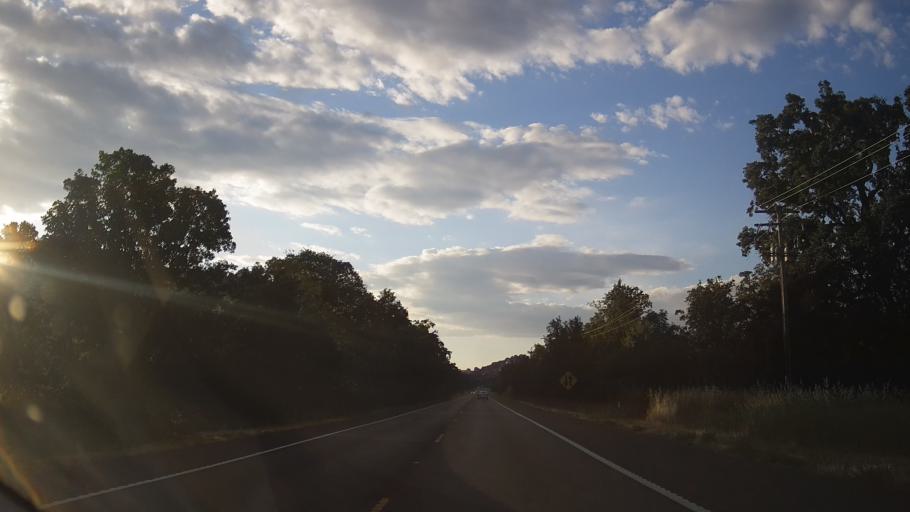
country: US
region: California
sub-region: Mendocino County
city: Talmage
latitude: 39.0472
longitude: -123.1523
